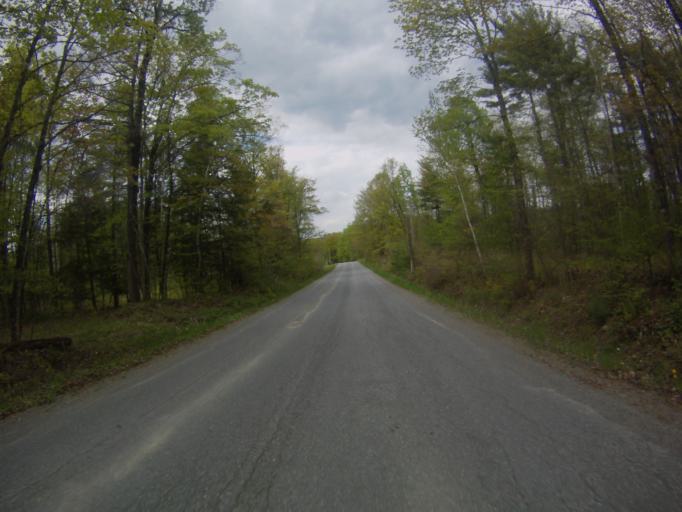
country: US
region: New York
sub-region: Essex County
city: Ticonderoga
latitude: 43.9240
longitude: -73.5036
